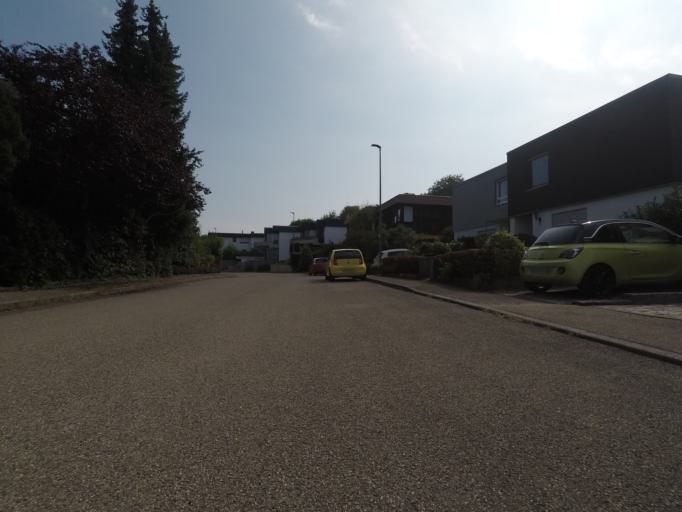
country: DE
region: Baden-Wuerttemberg
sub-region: Regierungsbezirk Stuttgart
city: Winterbach
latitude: 48.7931
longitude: 9.4851
